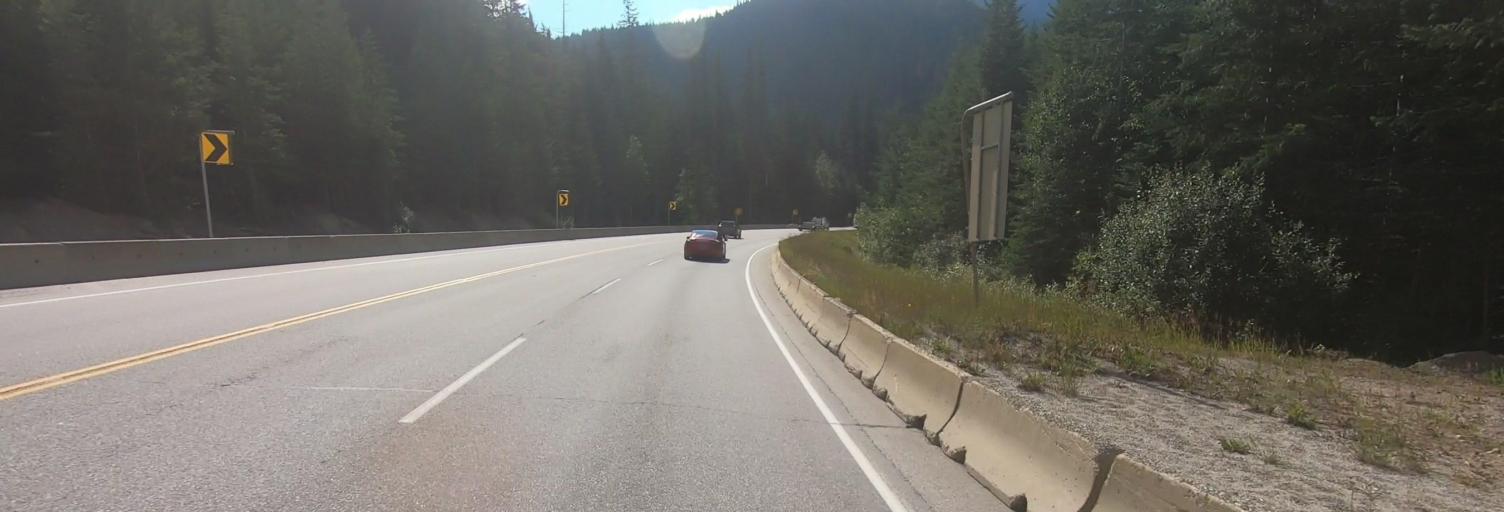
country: CA
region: British Columbia
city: Golden
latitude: 51.3464
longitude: -117.4345
